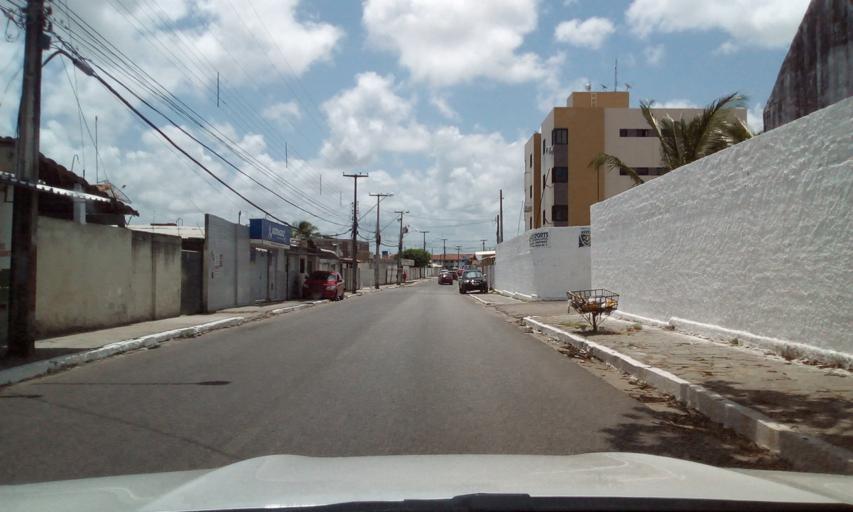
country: BR
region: Paraiba
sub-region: Joao Pessoa
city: Joao Pessoa
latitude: -7.1848
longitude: -34.8673
